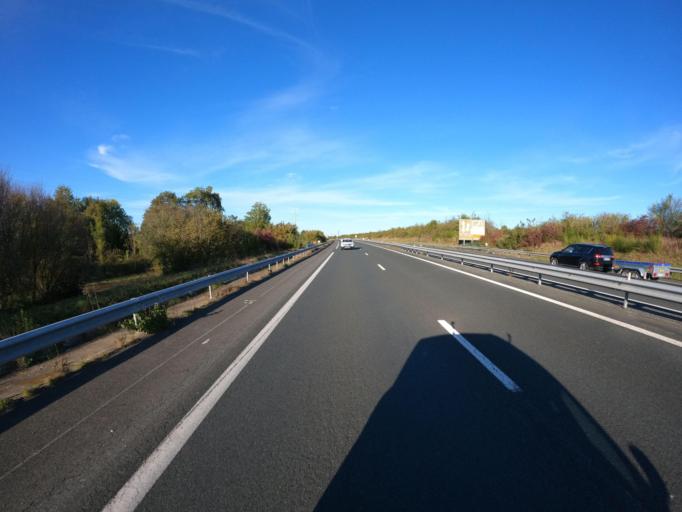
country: FR
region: Pays de la Loire
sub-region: Departement de Maine-et-Loire
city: Mazieres-en-Mauges
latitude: 47.0384
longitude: -0.8466
